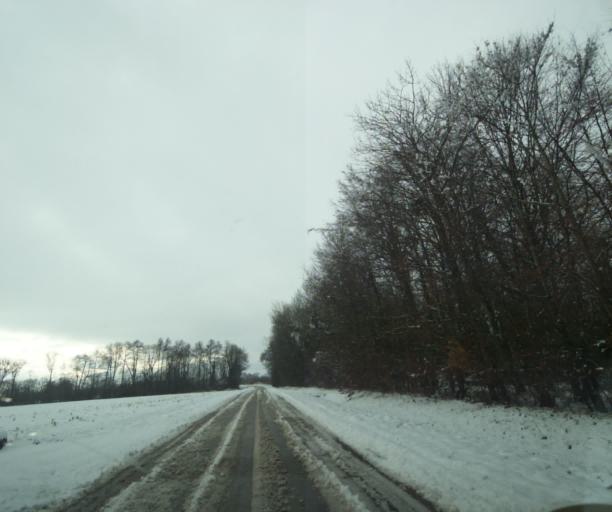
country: FR
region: Champagne-Ardenne
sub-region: Departement de la Haute-Marne
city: Montier-en-Der
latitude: 48.4756
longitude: 4.6642
